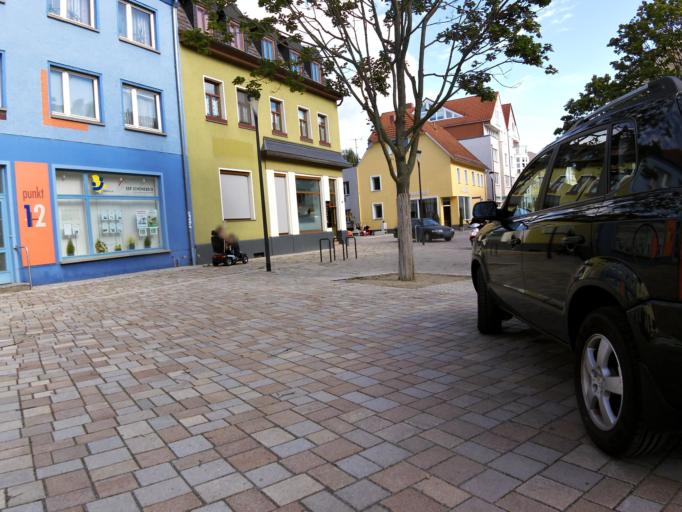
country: DE
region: Saxony-Anhalt
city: Schonebeck
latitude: 52.0214
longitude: 11.7384
